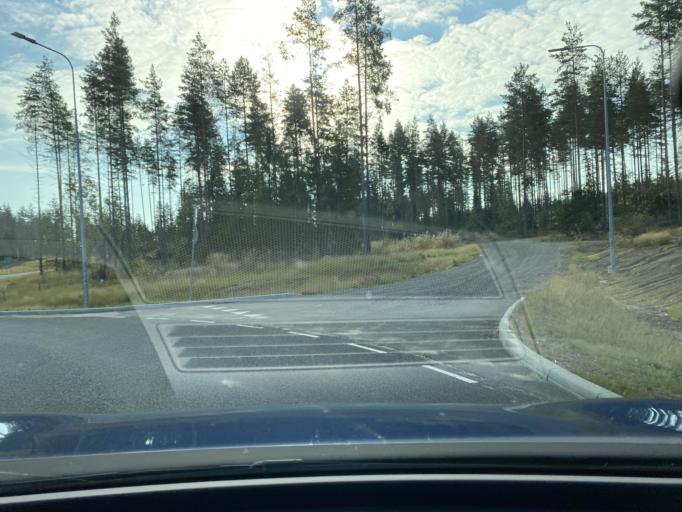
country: FI
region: Kymenlaakso
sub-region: Kouvola
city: Elimaeki
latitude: 60.8749
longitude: 26.5022
